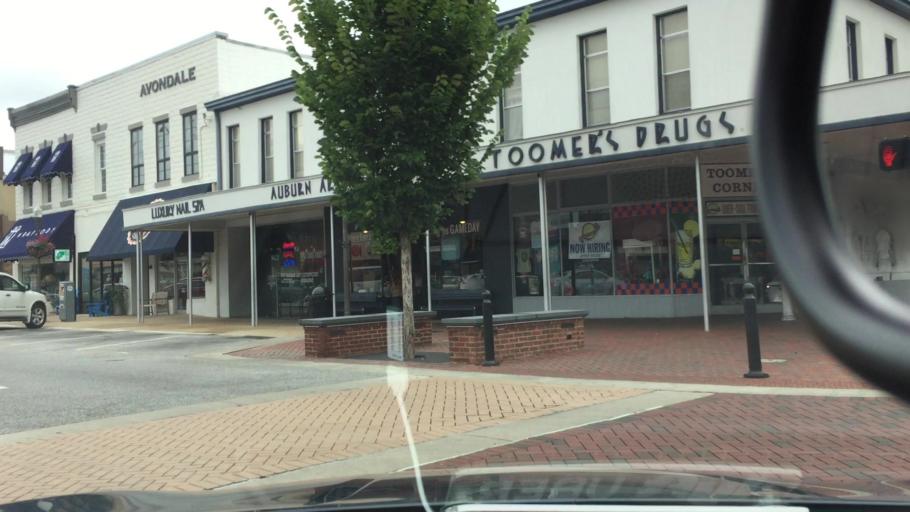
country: US
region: Alabama
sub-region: Lee County
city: Auburn
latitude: 32.6066
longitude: -85.4818
